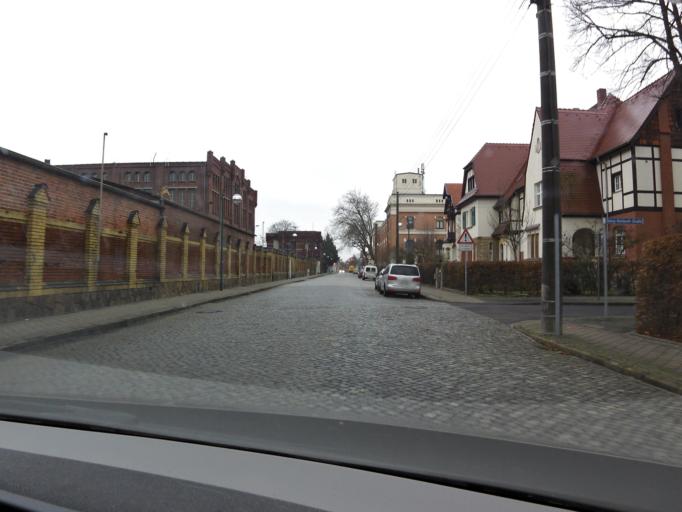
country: DE
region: Saxony
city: Markranstadt
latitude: 51.3268
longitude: 12.2534
